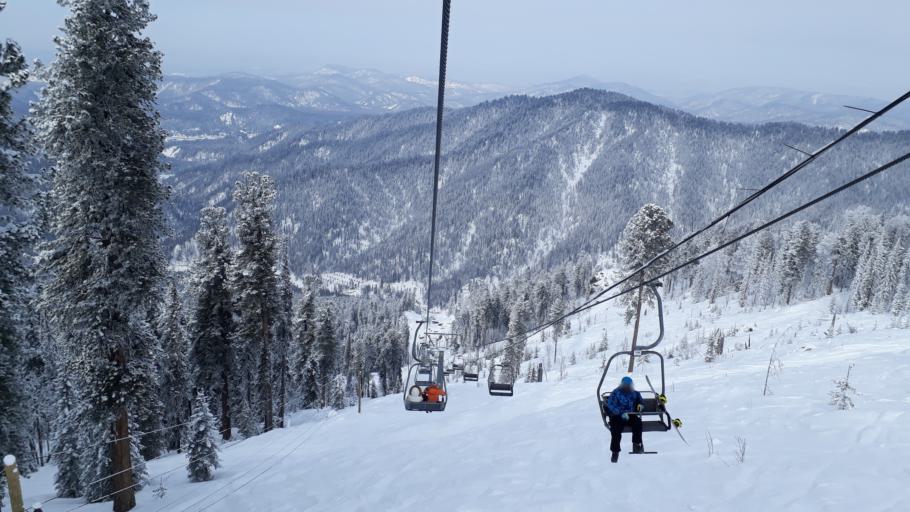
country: RU
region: Altay
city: Iogach
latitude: 51.7309
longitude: 87.3002
